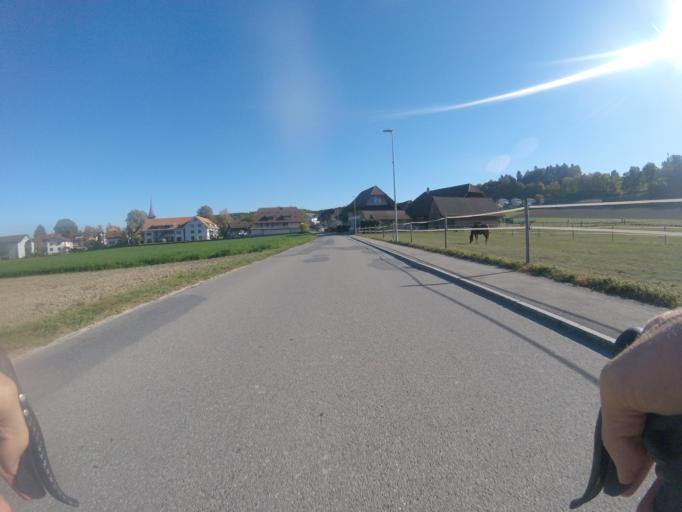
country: CH
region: Bern
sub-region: Seeland District
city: Schupfen
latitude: 47.0389
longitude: 7.3734
